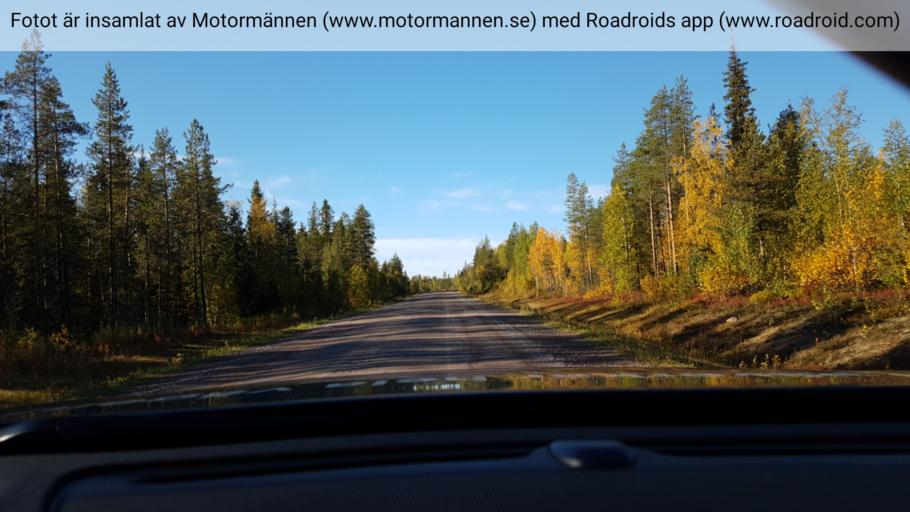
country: SE
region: Norrbotten
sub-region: Alvsbyns Kommun
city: AElvsbyn
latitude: 66.2680
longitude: 20.9850
